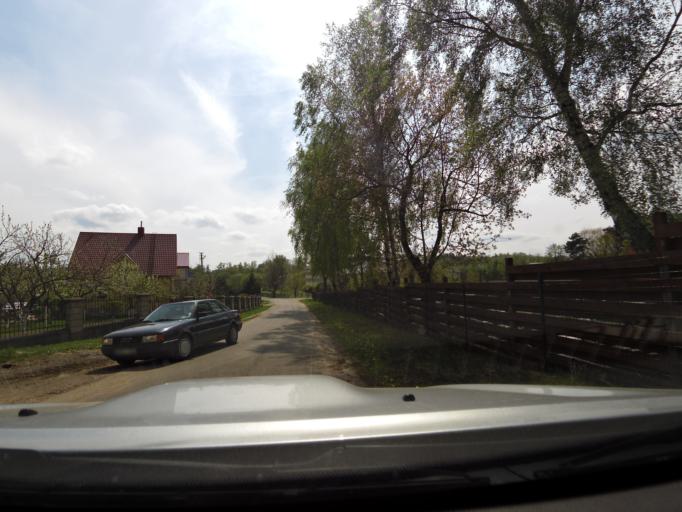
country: LT
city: Salcininkai
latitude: 54.4376
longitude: 25.3001
